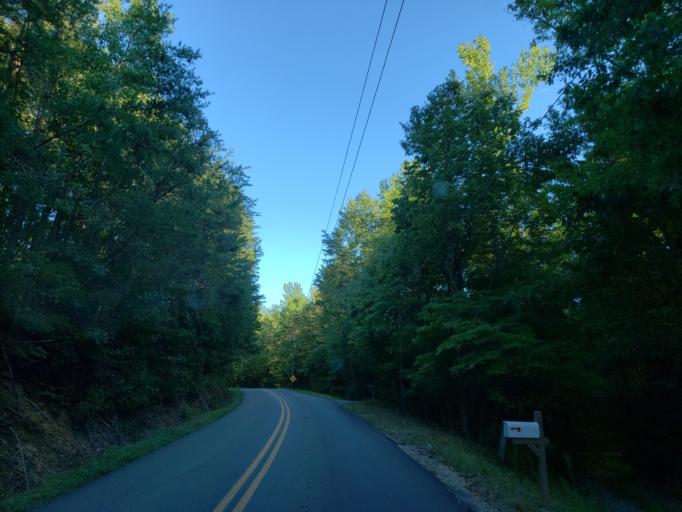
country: US
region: Georgia
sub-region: Bartow County
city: Rydal
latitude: 34.4147
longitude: -84.6924
